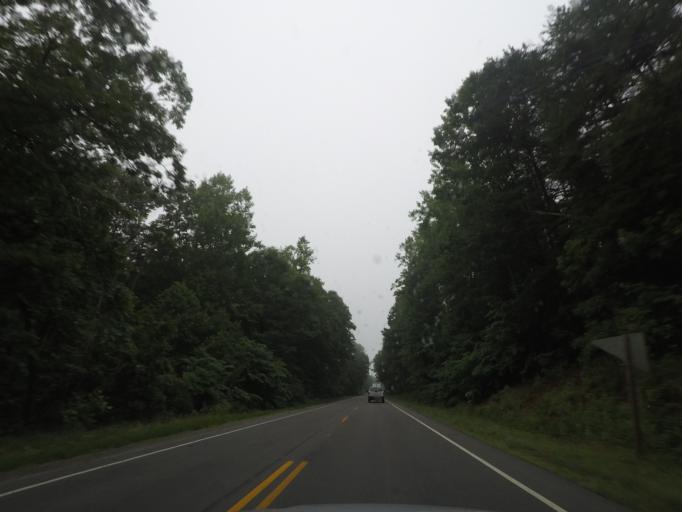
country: US
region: Virginia
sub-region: Buckingham County
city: Buckingham
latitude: 37.4612
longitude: -78.4672
